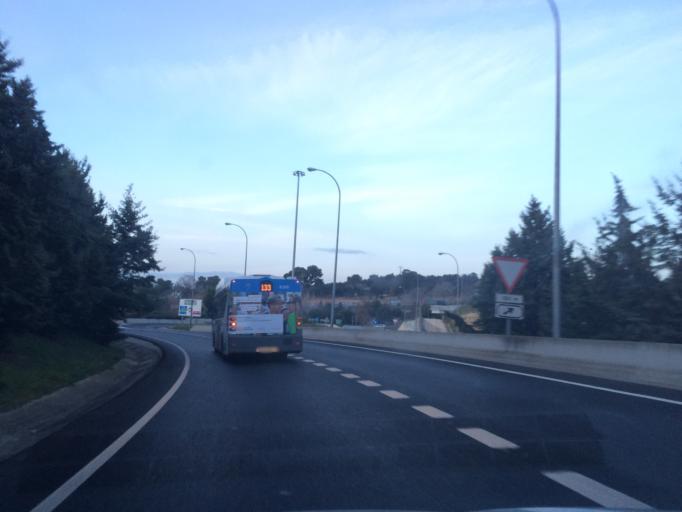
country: ES
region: Madrid
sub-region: Provincia de Madrid
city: Moncloa-Aravaca
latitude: 40.4527
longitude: -3.7397
